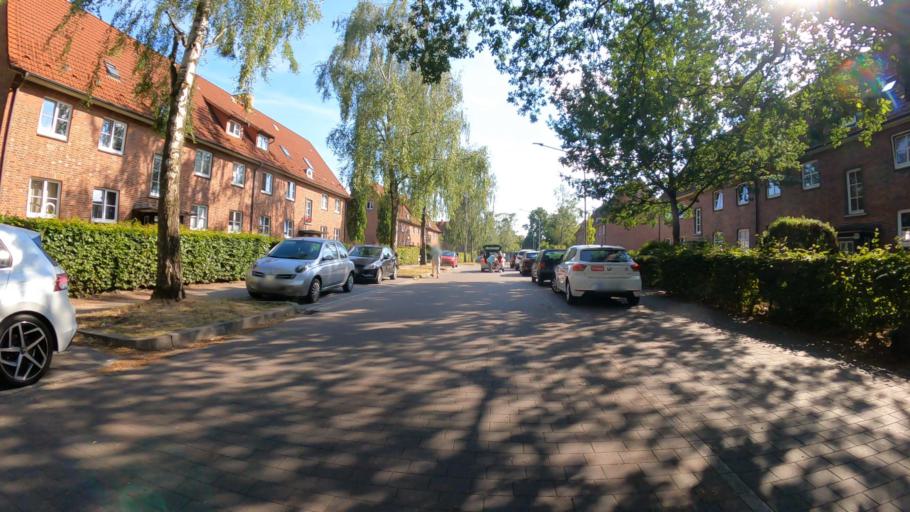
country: DE
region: Schleswig-Holstein
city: Norderstedt
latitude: 53.6837
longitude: 9.9819
